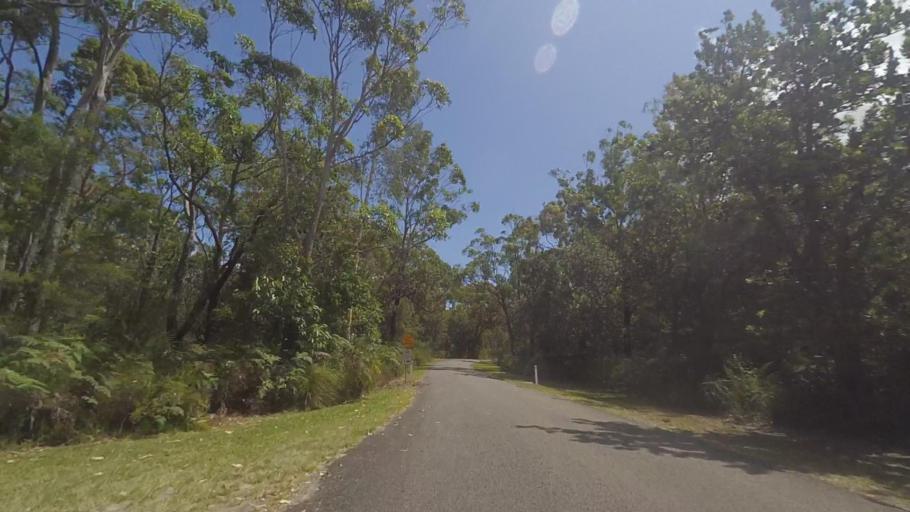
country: AU
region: New South Wales
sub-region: Great Lakes
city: Bulahdelah
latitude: -32.5032
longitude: 152.3082
